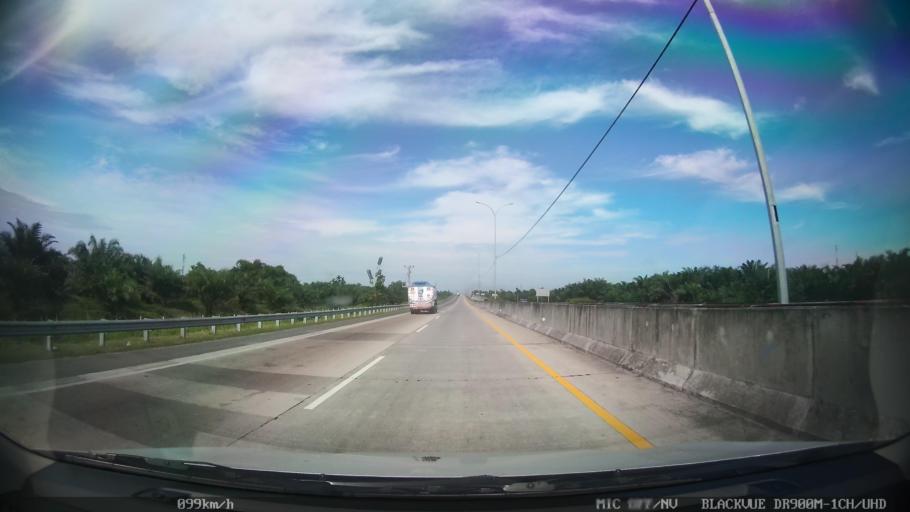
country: ID
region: North Sumatra
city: Sunggal
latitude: 3.6379
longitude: 98.5998
